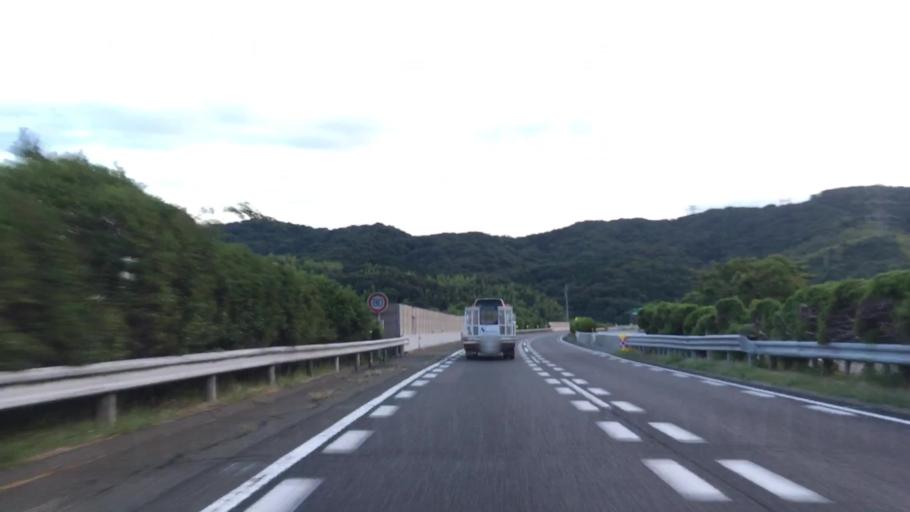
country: JP
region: Yamaguchi
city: Shimonoseki
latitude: 33.9311
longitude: 130.9951
